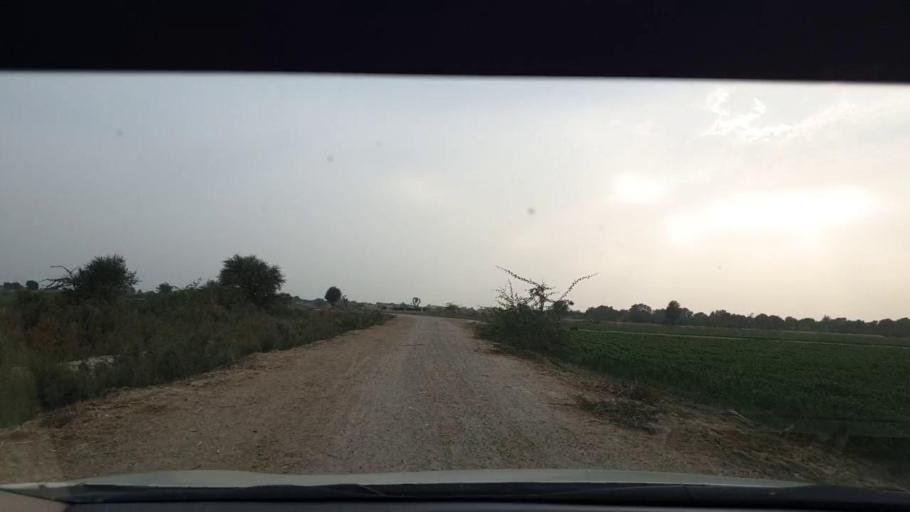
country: PK
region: Sindh
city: Jhol
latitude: 25.9038
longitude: 68.8014
